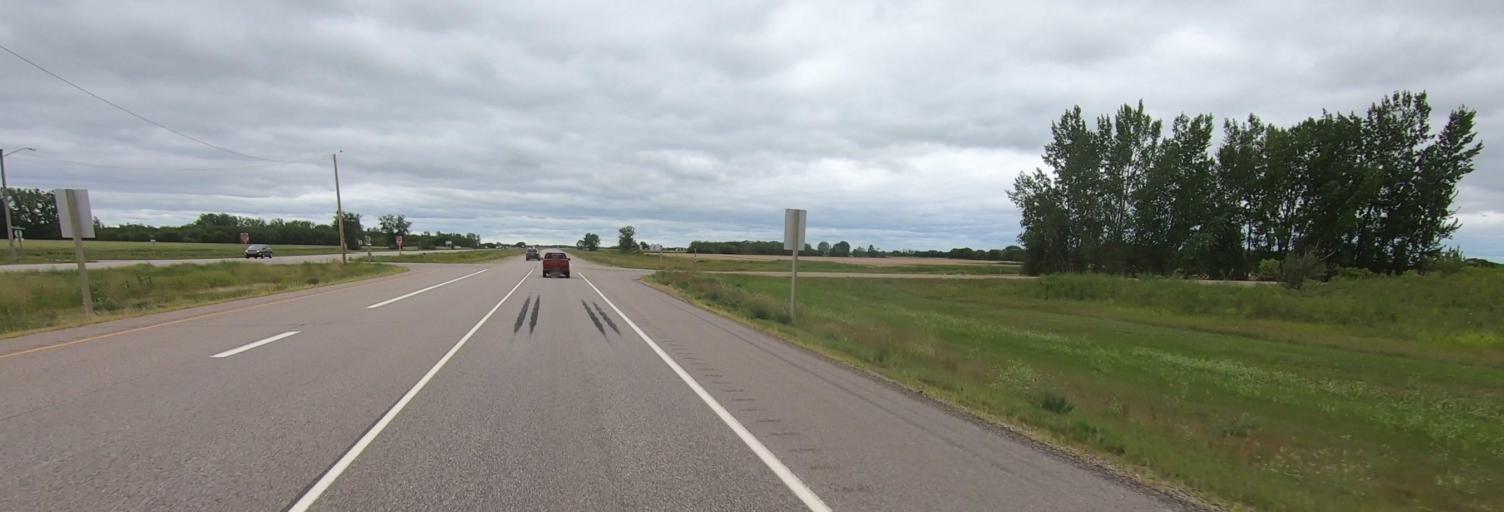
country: CA
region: Manitoba
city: Portage la Prairie
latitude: 49.9700
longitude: -98.7892
